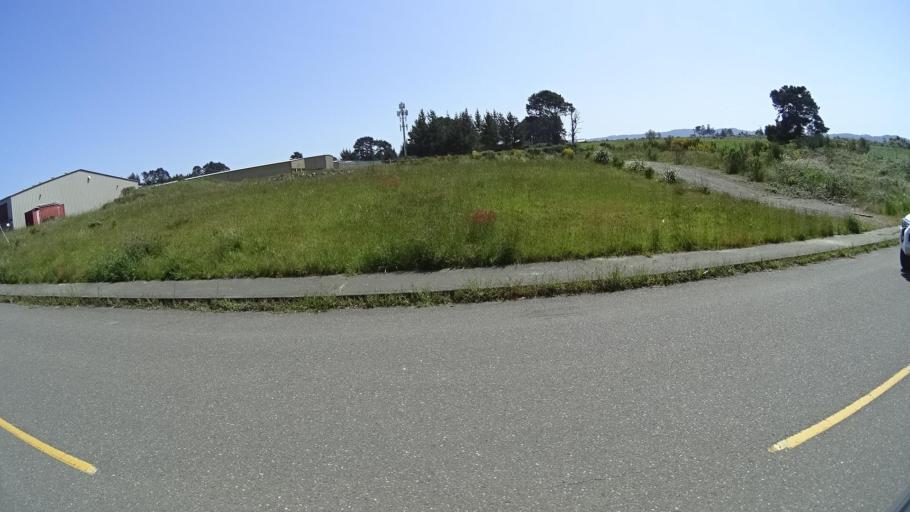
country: US
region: California
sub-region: Humboldt County
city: Hydesville
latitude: 40.5630
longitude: -124.1330
